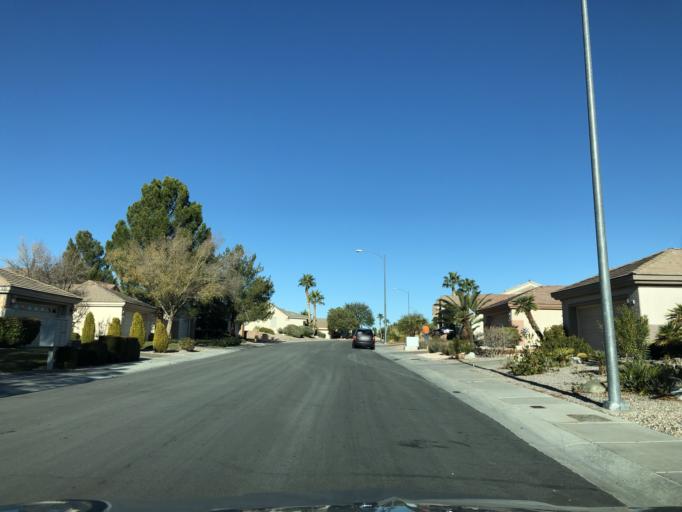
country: US
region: Nevada
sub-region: Clark County
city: Whitney
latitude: 36.0068
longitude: -115.0723
